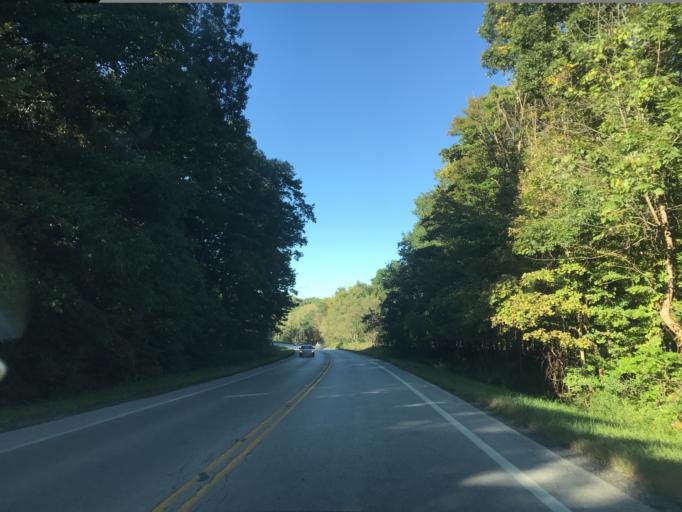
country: US
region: Ohio
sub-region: Ashtabula County
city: Geneva
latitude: 41.7520
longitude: -80.9412
